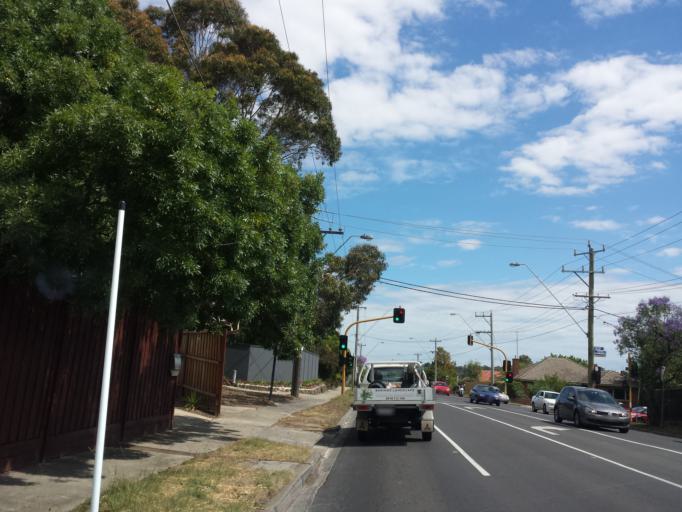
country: AU
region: Victoria
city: Rosanna
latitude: -37.7448
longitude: 145.0718
